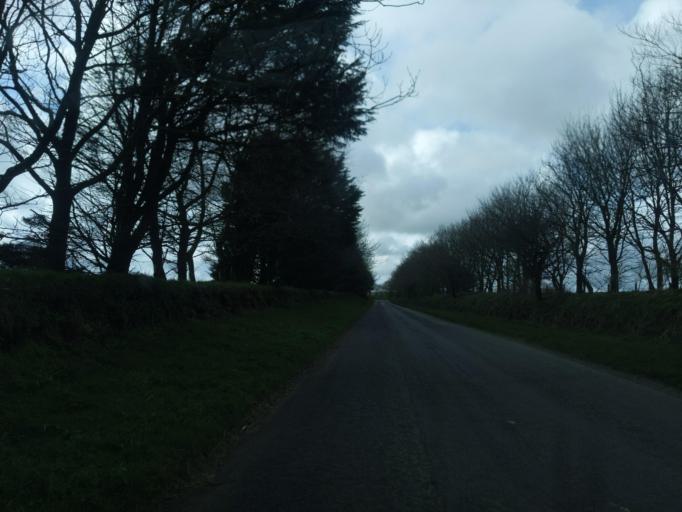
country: GB
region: England
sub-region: Cornwall
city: Camelford
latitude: 50.6246
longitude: -4.5767
